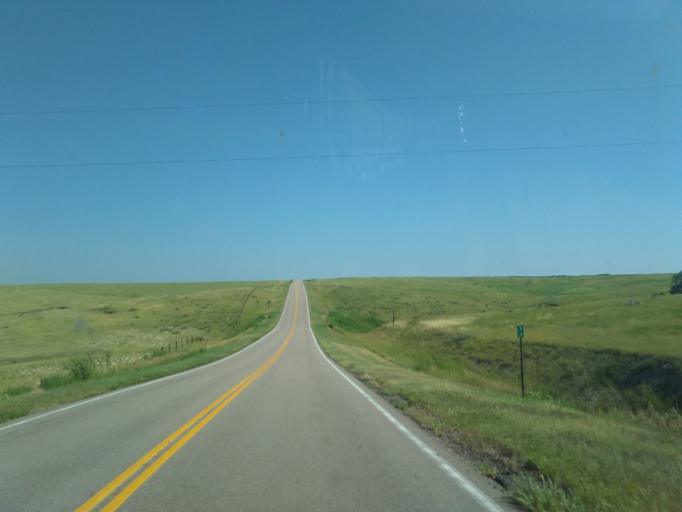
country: US
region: Nebraska
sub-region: Dundy County
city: Benkelman
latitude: 39.9447
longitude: -101.5414
